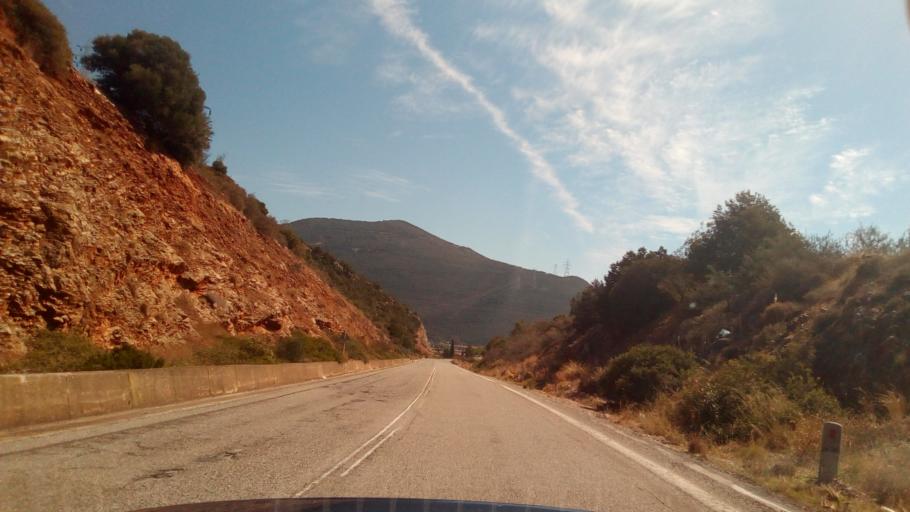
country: GR
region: West Greece
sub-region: Nomos Achaias
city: Selianitika
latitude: 38.3688
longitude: 22.1120
